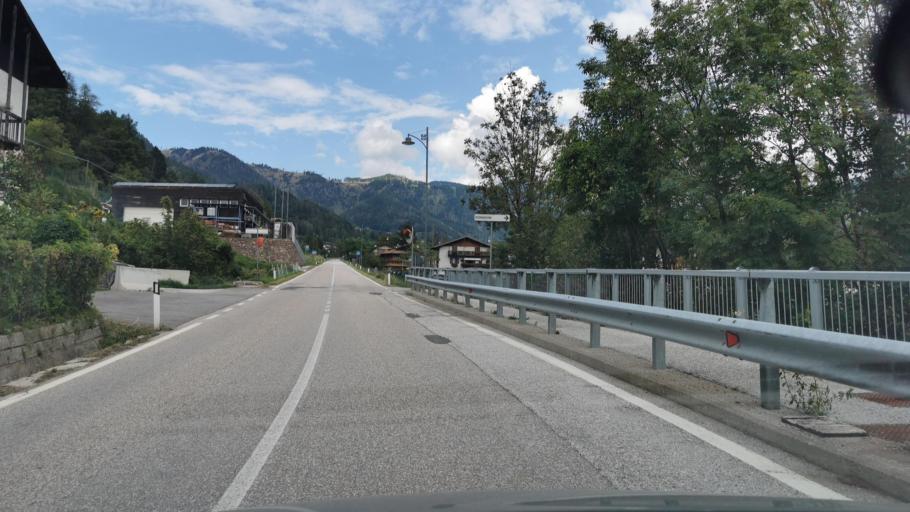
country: IT
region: Trentino-Alto Adige
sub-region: Provincia di Trento
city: Sant'Orsola
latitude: 46.1015
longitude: 11.2976
